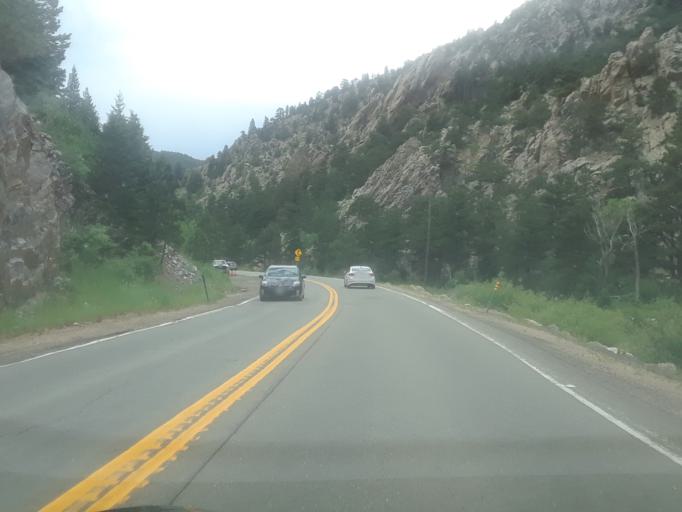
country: US
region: Colorado
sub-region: Boulder County
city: Coal Creek
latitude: 39.8826
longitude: -105.3069
